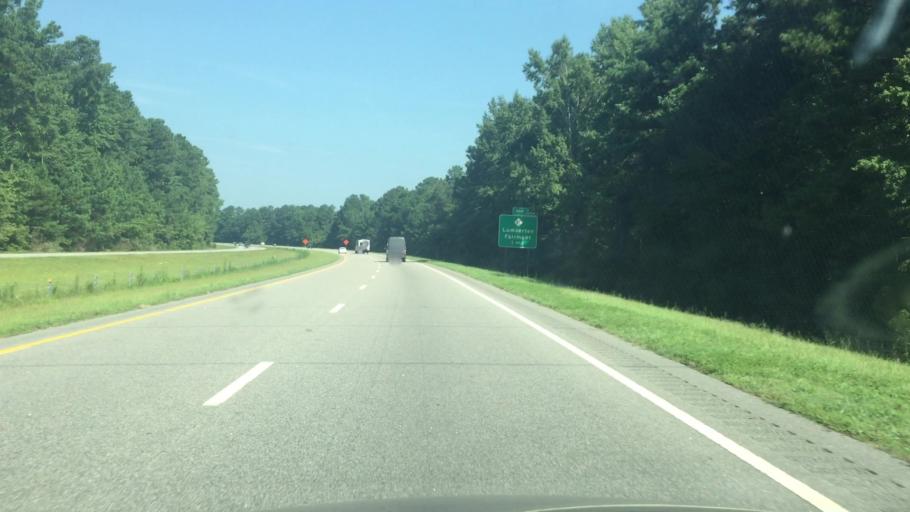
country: US
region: North Carolina
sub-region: Robeson County
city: Lumberton
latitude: 34.5675
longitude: -79.0295
